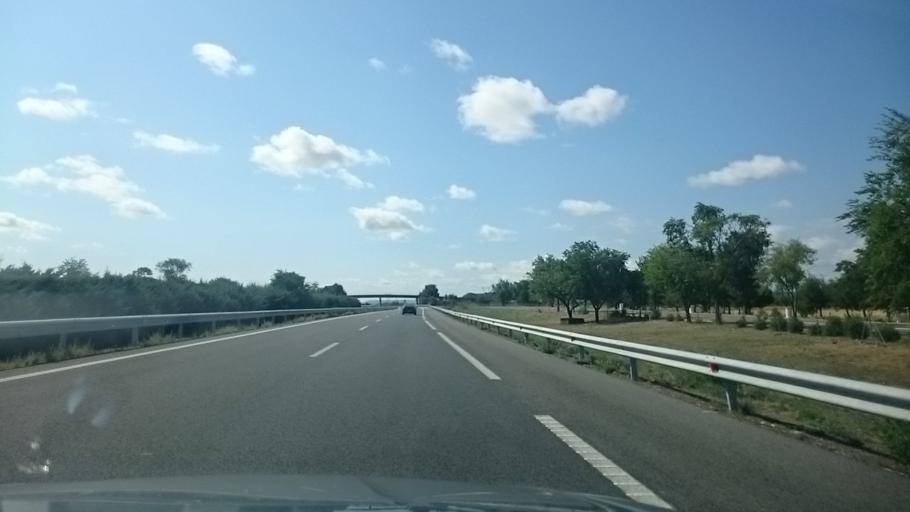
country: ES
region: Navarre
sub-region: Provincia de Navarra
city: Corella
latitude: 42.1170
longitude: -1.7387
